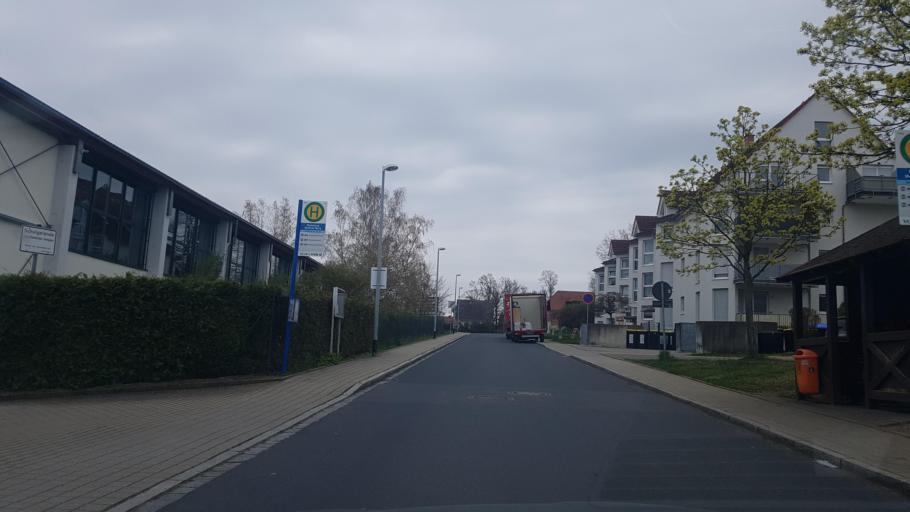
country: DE
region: Saxony
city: Radeburg
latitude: 51.2137
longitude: 13.7151
